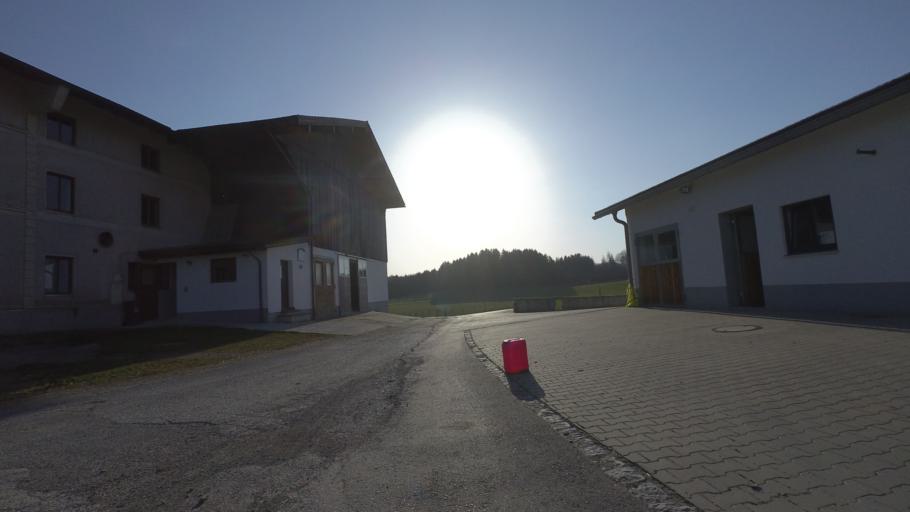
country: DE
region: Bavaria
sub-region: Upper Bavaria
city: Nussdorf
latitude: 47.9308
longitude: 12.5711
